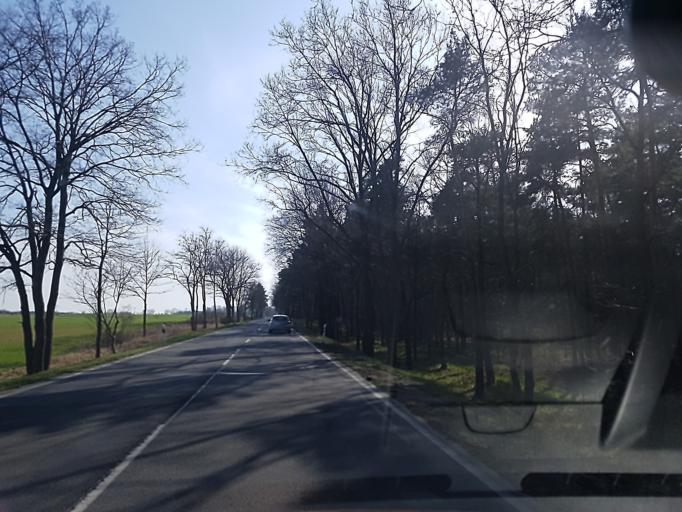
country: DE
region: Brandenburg
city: Calau
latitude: 51.7332
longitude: 13.9357
